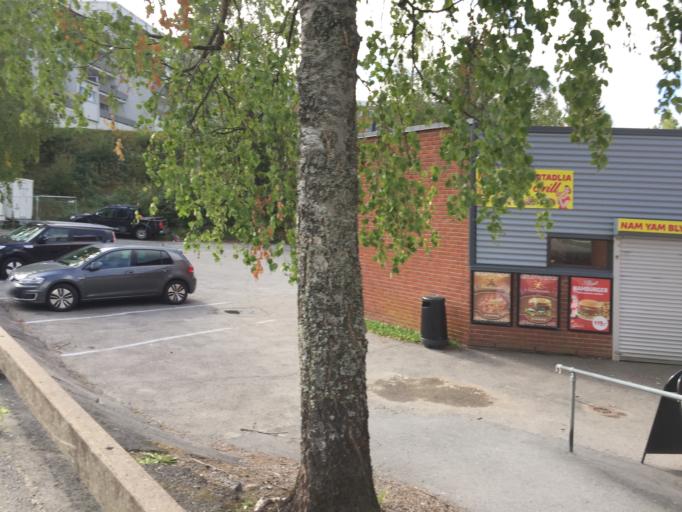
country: NO
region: Akershus
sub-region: Skedsmo
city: Lillestrom
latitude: 59.9310
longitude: 11.0361
